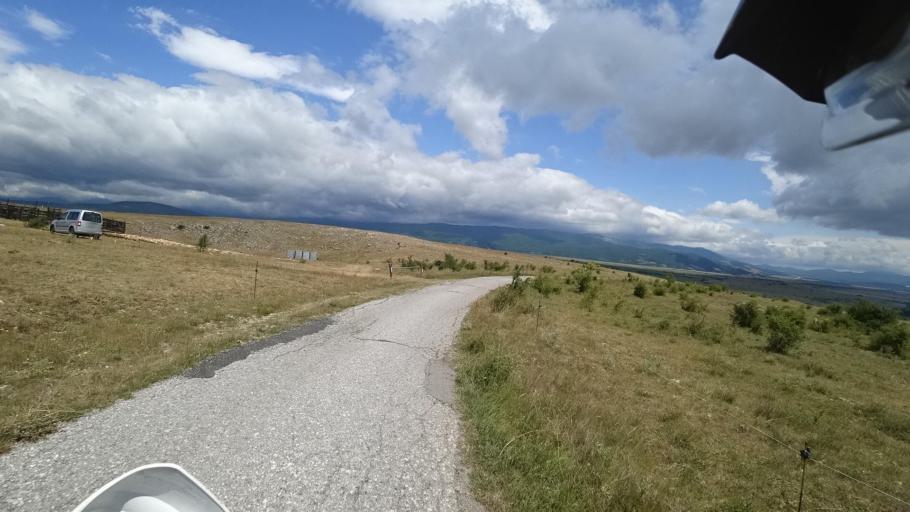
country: HR
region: Licko-Senjska
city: Jezerce
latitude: 44.6161
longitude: 15.6553
